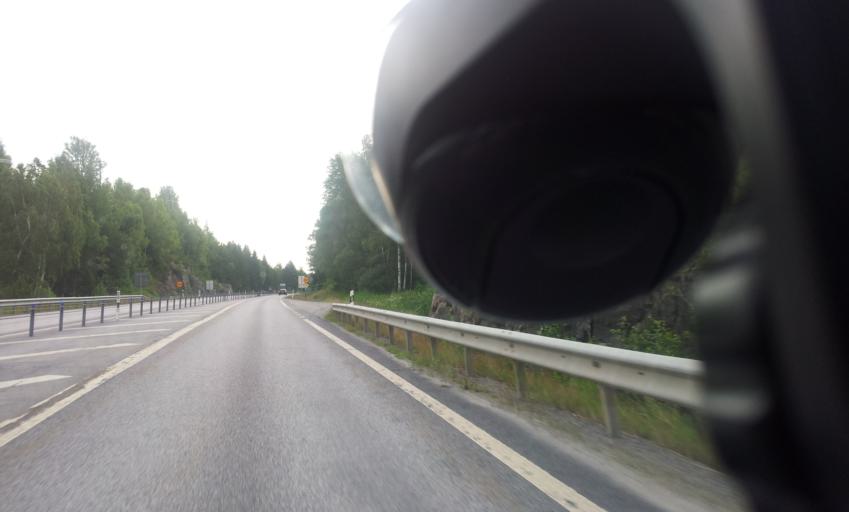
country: SE
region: OEstergoetland
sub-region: Valdemarsviks Kommun
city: Valdemarsvik
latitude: 58.1933
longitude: 16.5409
